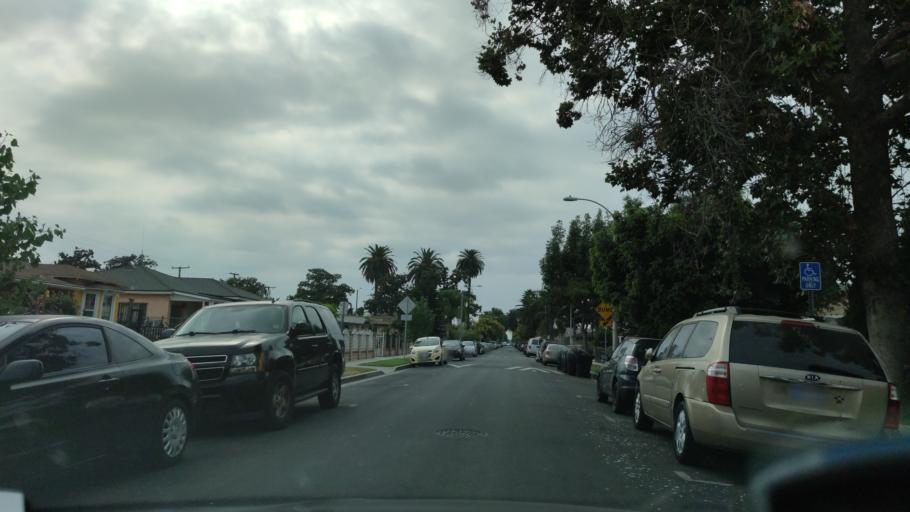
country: US
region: California
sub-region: Los Angeles County
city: Maywood
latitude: 33.9925
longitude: -118.1903
